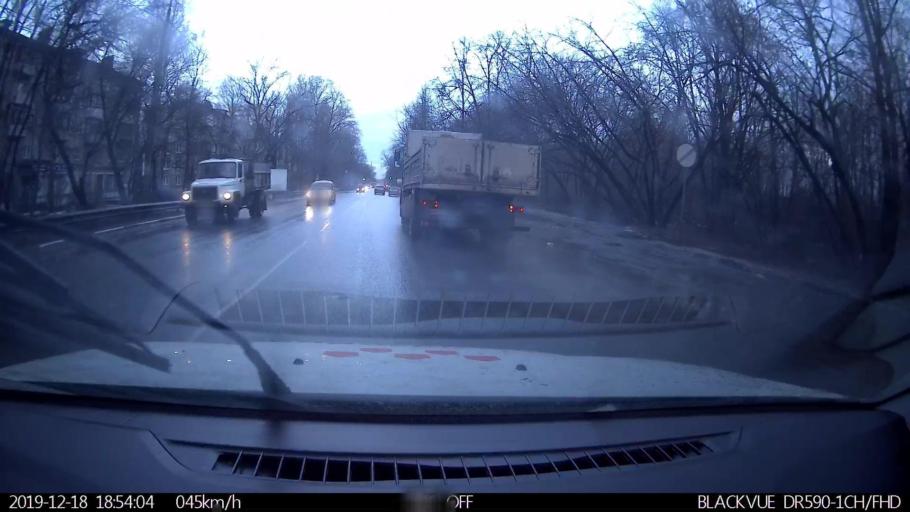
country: RU
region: Nizjnij Novgorod
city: Gorbatovka
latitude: 56.3367
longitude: 43.8471
